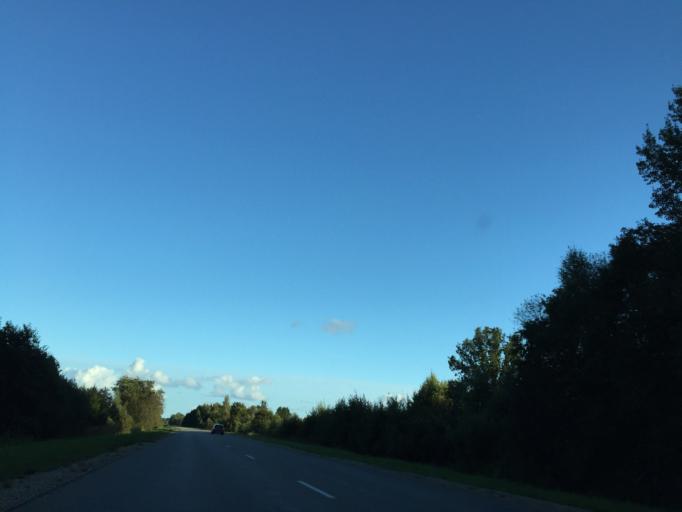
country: LV
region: Kuldigas Rajons
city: Kuldiga
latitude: 56.9491
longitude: 22.0145
